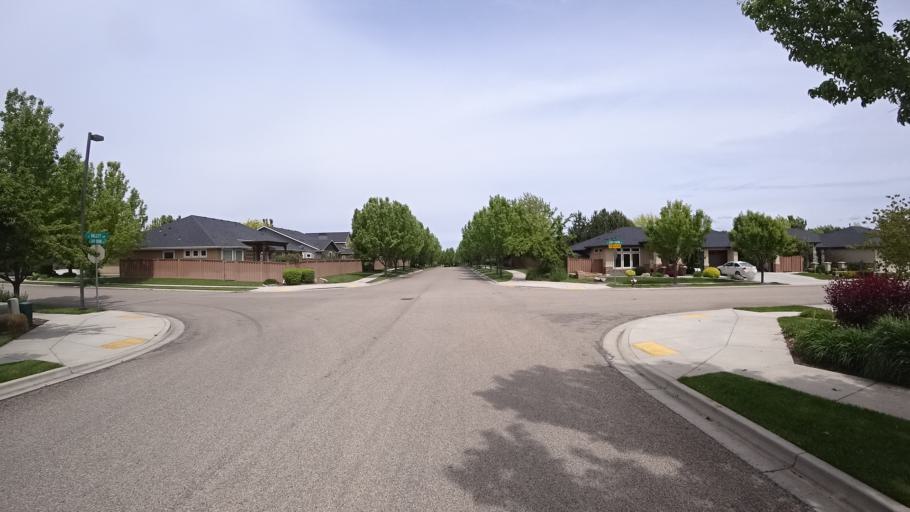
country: US
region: Idaho
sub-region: Ada County
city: Meridian
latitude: 43.5577
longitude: -116.3243
